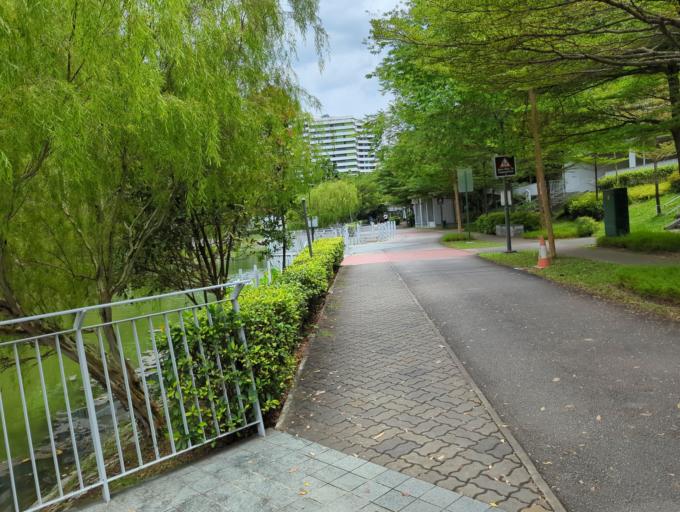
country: MY
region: Johor
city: Kampung Pasir Gudang Baru
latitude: 1.4093
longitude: 103.8970
